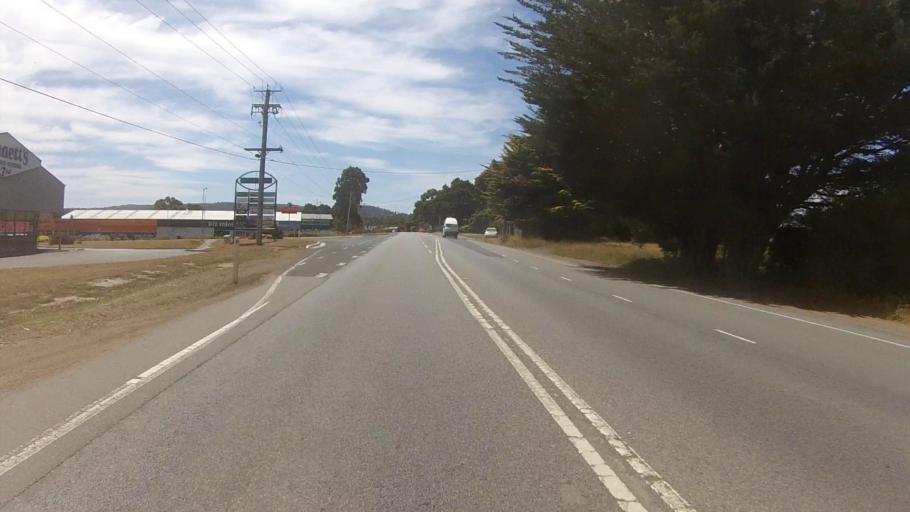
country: AU
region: Tasmania
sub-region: Kingborough
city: Kingston
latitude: -42.9832
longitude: 147.2944
